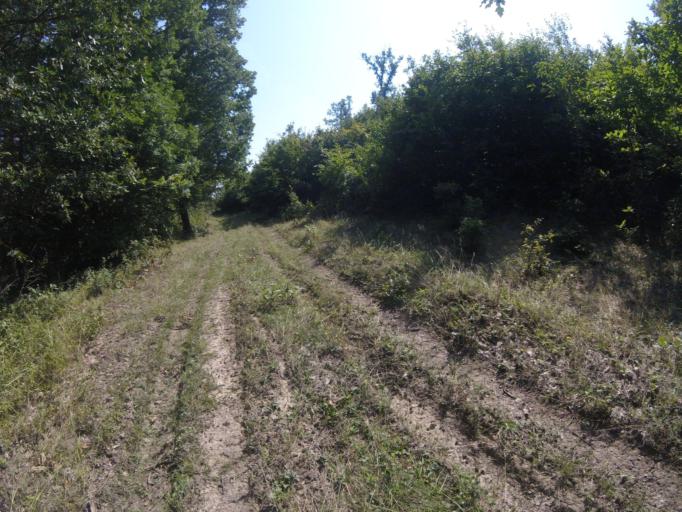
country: HU
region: Nograd
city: Bujak
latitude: 47.8965
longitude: 19.5133
